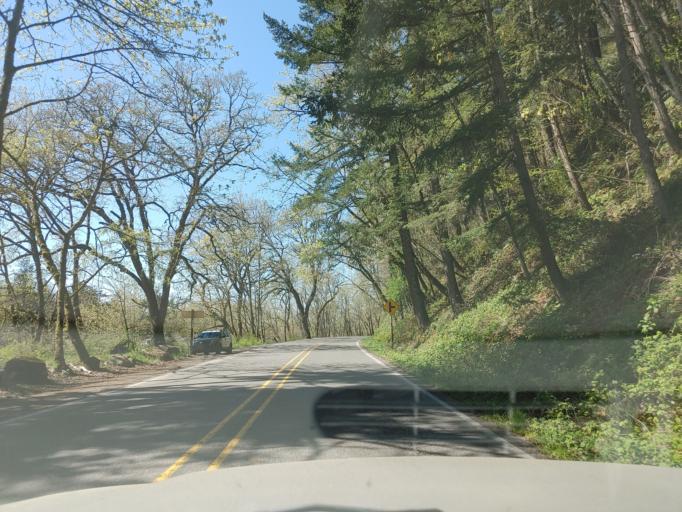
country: US
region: Oregon
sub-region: Multnomah County
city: Troutdale
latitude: 45.5394
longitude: -122.3773
